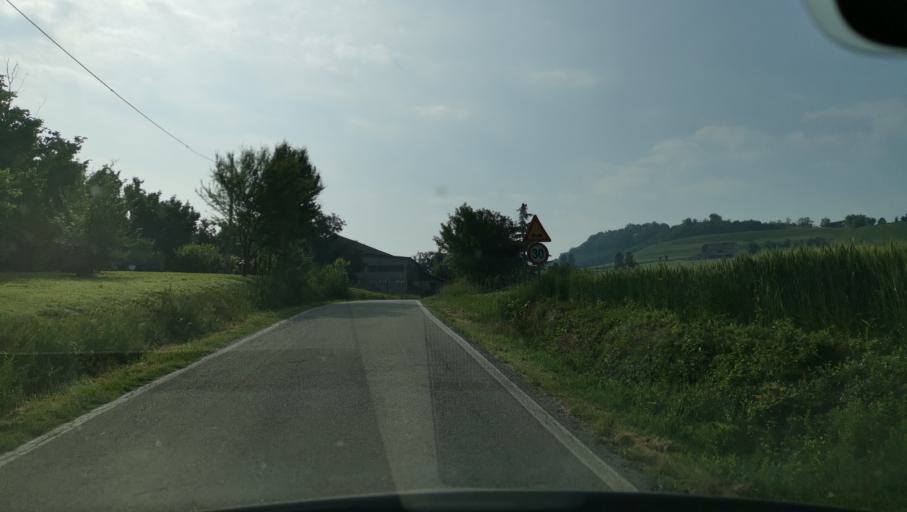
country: IT
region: Piedmont
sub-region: Provincia di Alessandria
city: Castelletto Merli
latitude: 45.0625
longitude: 8.2409
